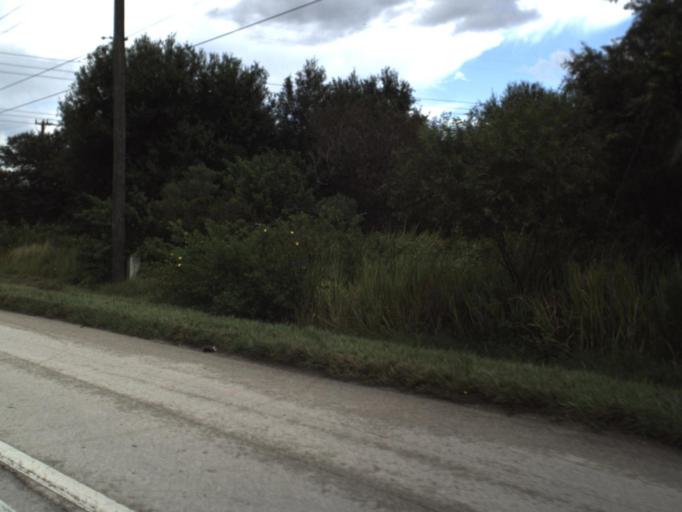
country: US
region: Florida
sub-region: Polk County
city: Mulberry
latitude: 27.8647
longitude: -81.9734
